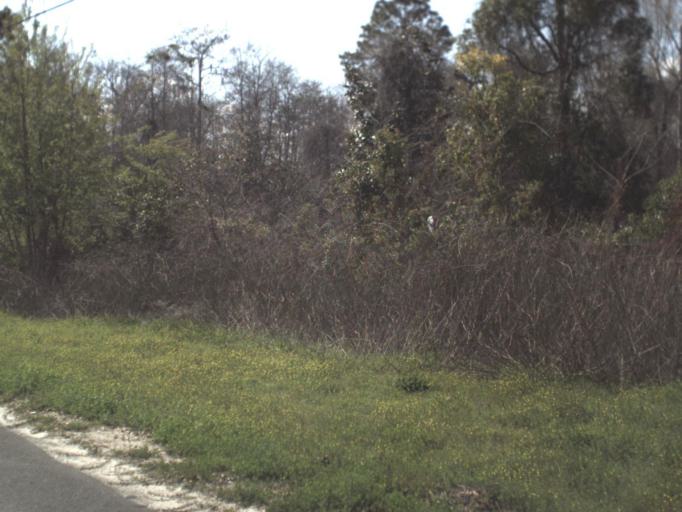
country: US
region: Florida
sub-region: Wakulla County
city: Crawfordville
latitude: 30.0726
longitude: -84.4384
